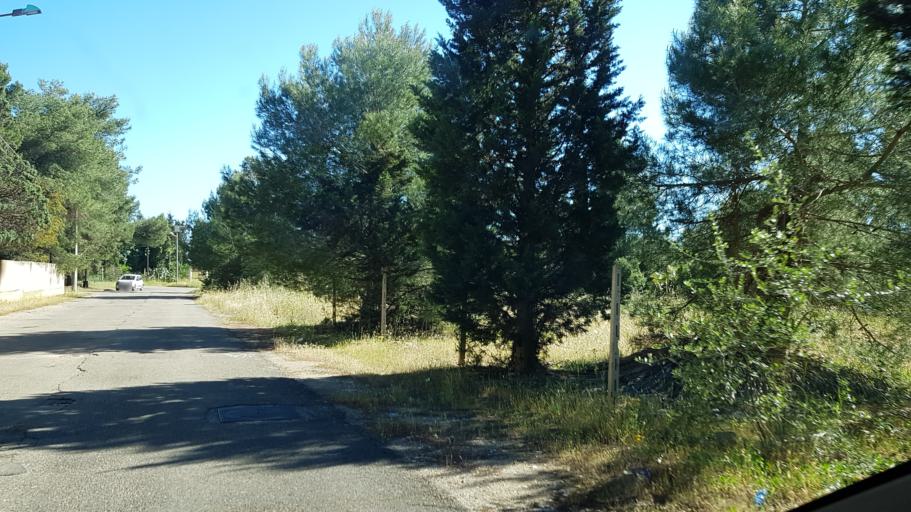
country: IT
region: Apulia
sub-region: Provincia di Brindisi
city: Torchiarolo
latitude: 40.5243
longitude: 18.0754
